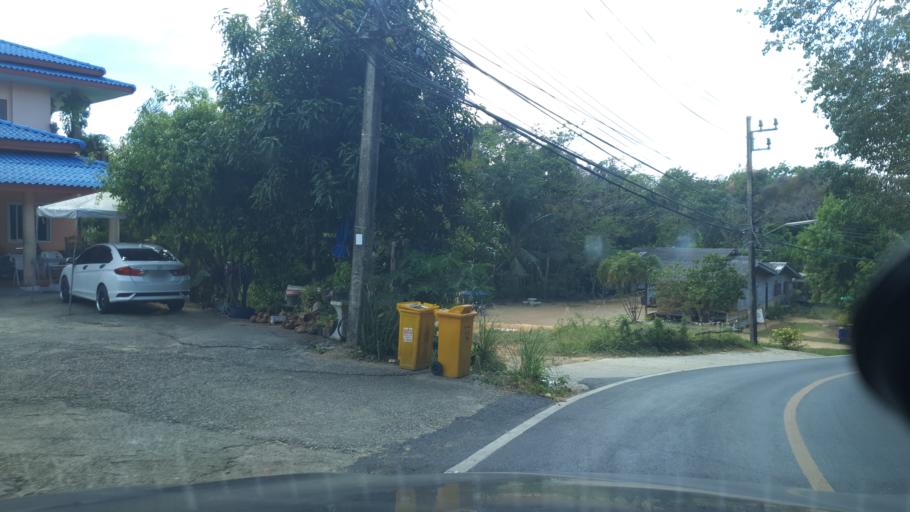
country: TH
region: Phuket
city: Thalang
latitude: 8.0627
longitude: 98.2825
